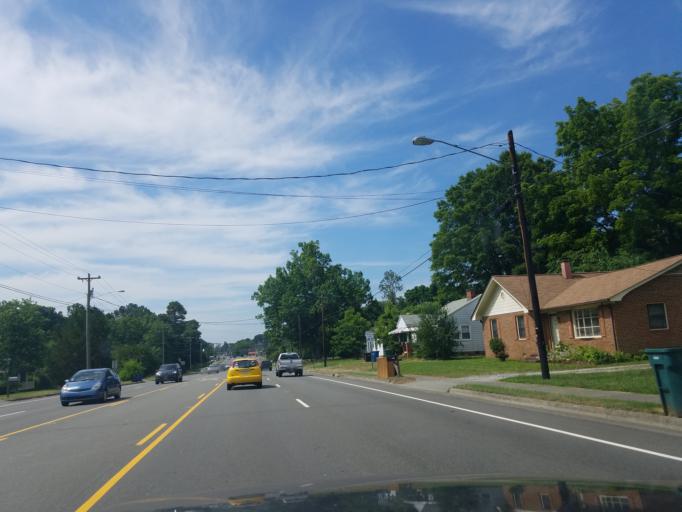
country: US
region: North Carolina
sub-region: Durham County
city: Durham
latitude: 36.0426
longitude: -78.9296
